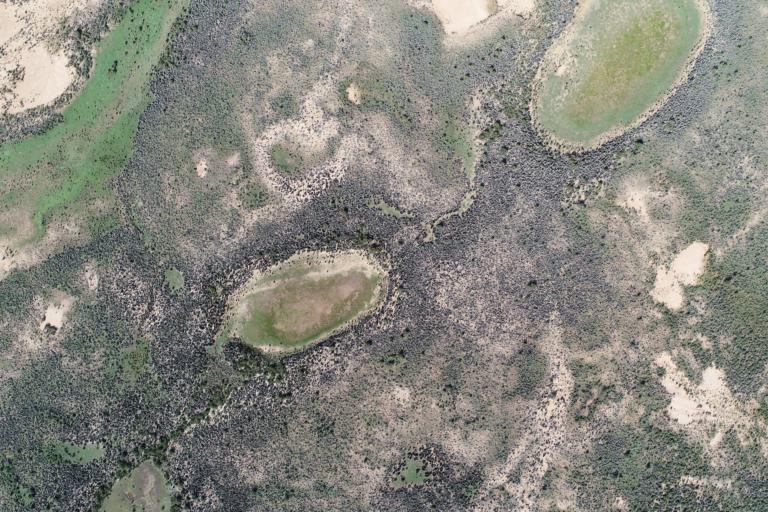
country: BO
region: La Paz
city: Curahuara de Carangas
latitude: -17.3015
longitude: -68.5100
